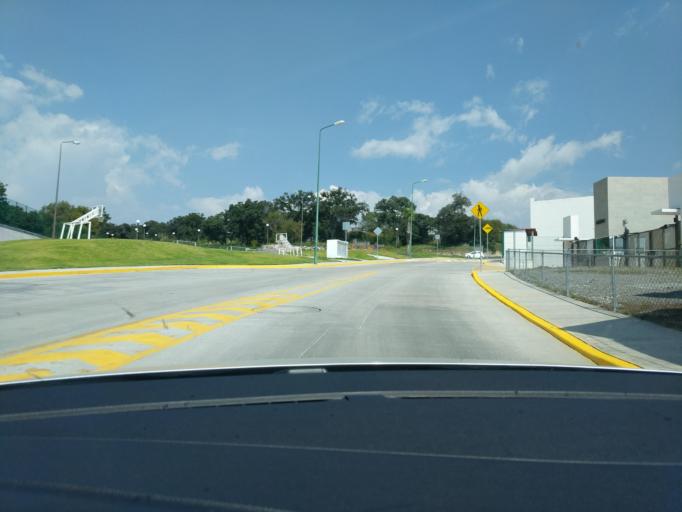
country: MX
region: Puebla
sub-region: Puebla
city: Galaxia la Calera
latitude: 19.0077
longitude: -98.1417
